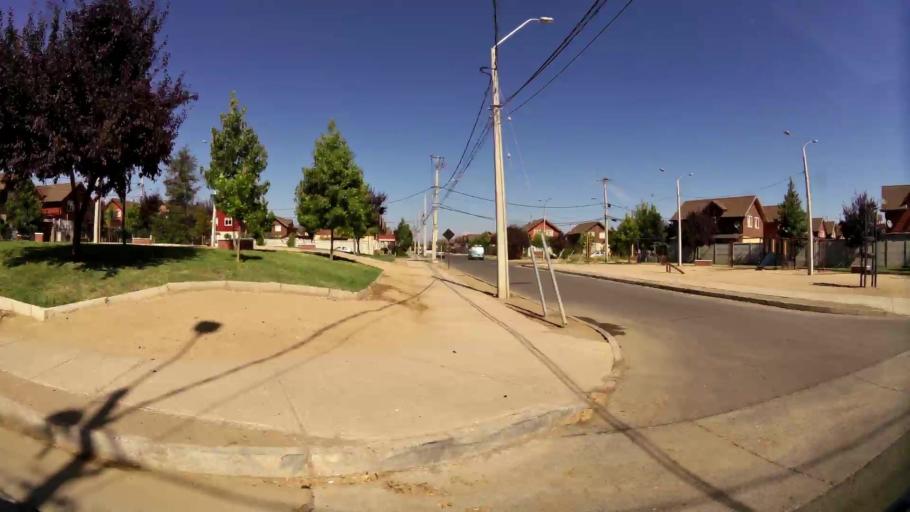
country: CL
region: Maule
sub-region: Provincia de Talca
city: Talca
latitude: -35.4188
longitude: -71.6167
